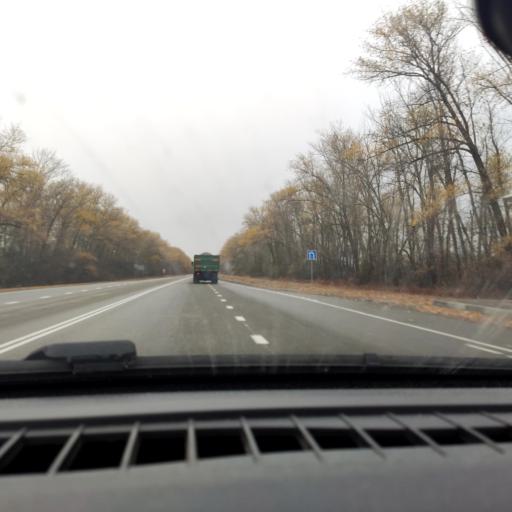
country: RU
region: Voronezj
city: Ostrogozhsk
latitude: 50.9782
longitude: 38.9938
